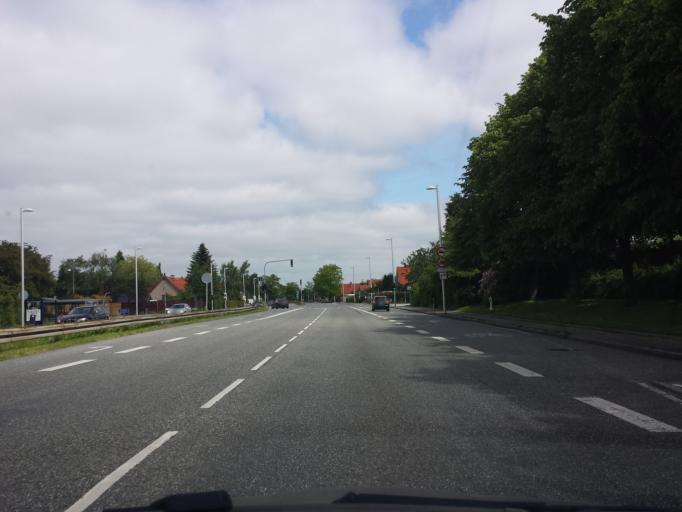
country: DK
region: Capital Region
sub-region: Glostrup Kommune
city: Glostrup
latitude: 55.6738
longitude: 12.3951
